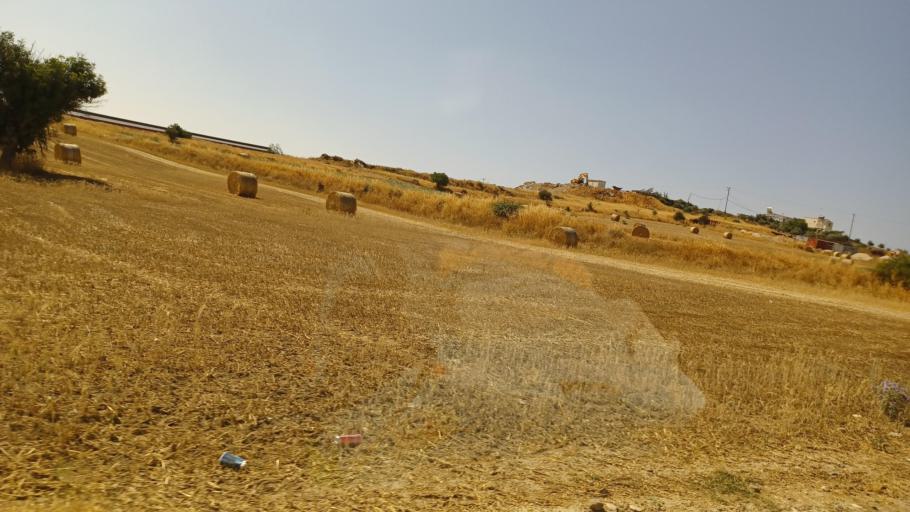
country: CY
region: Larnaka
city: Athienou
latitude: 35.0471
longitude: 33.5362
